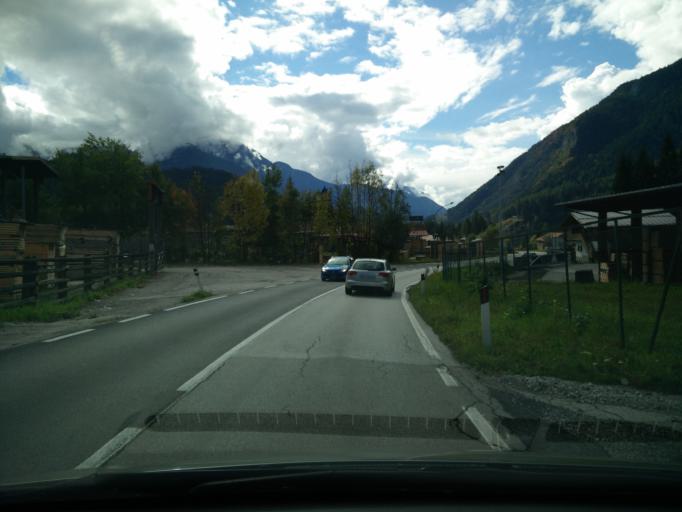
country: IT
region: Veneto
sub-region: Provincia di Belluno
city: Vigo di Cadore
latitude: 46.5144
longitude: 12.4636
